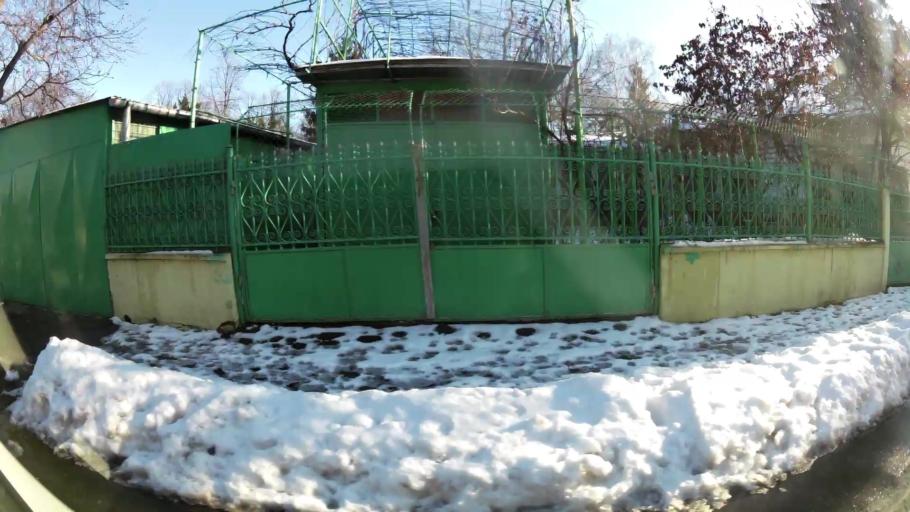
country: RO
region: Bucuresti
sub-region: Municipiul Bucuresti
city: Bucuresti
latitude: 44.4013
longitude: 26.0937
